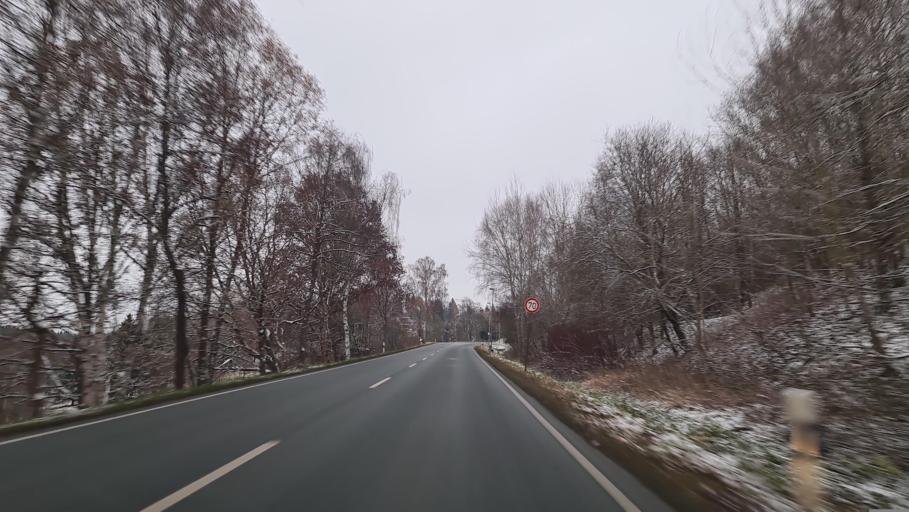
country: DE
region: Saxony
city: Markneukirchen
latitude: 50.3128
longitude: 12.3125
